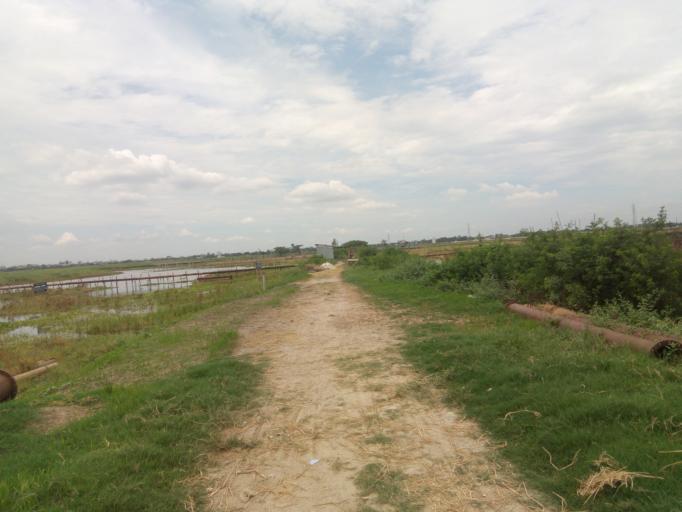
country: BD
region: Dhaka
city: Paltan
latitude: 23.7270
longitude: 90.4607
